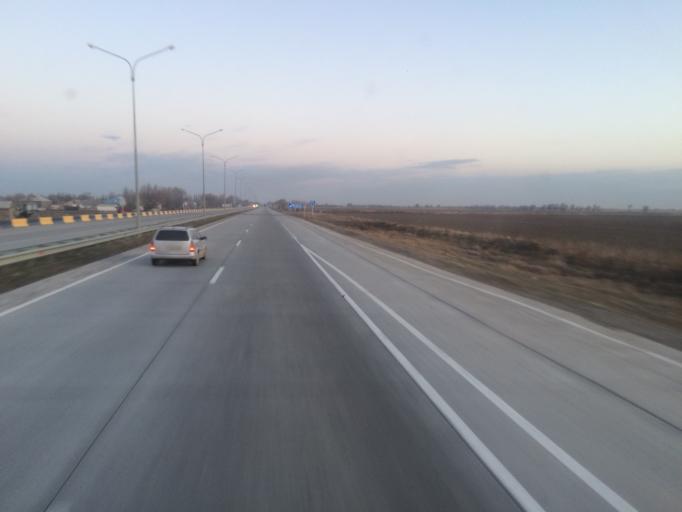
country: KZ
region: Ongtustik Qazaqstan
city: Shayan
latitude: 42.9628
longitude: 68.8849
